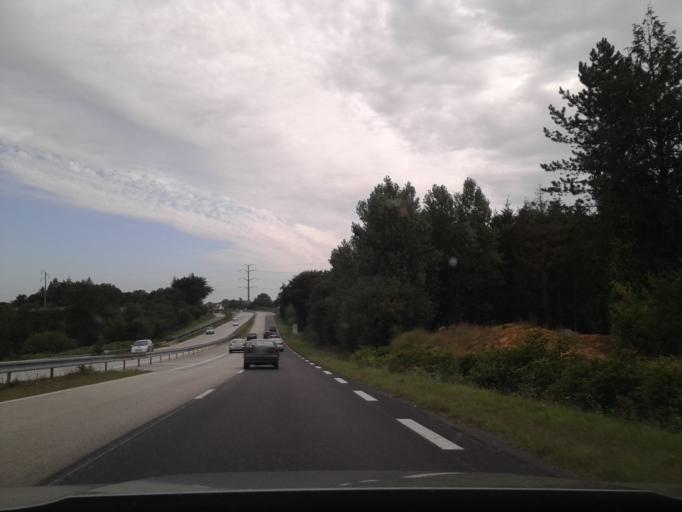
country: FR
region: Lower Normandy
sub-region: Departement de la Manche
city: La Glacerie
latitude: 49.5928
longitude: -1.5958
